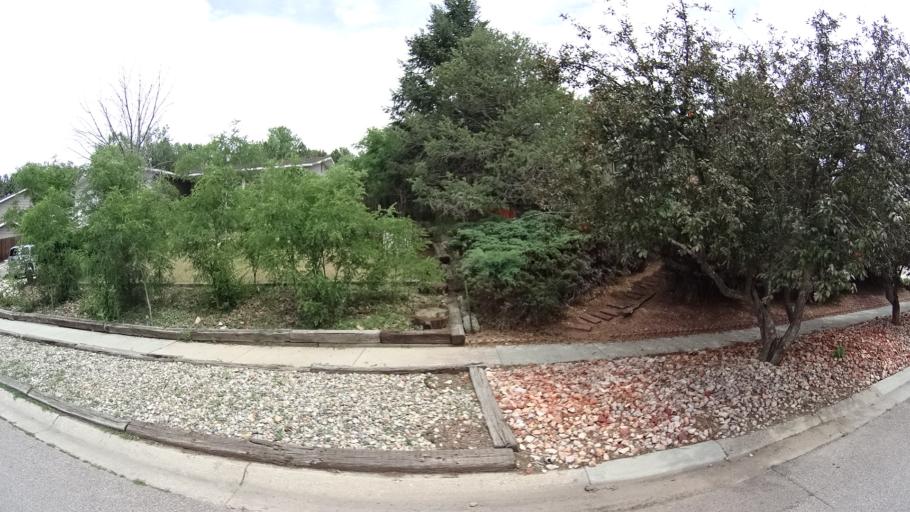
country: US
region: Colorado
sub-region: El Paso County
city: Colorado Springs
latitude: 38.8572
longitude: -104.8636
